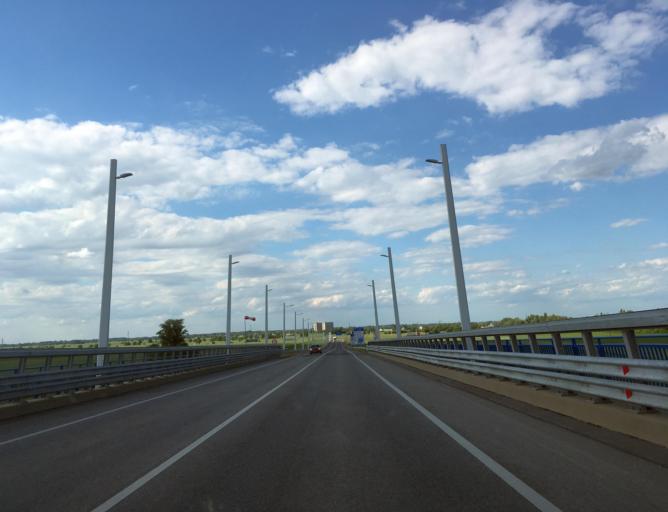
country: HU
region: Komarom-Esztergom
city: Komarom
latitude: 47.7592
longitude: 18.0846
